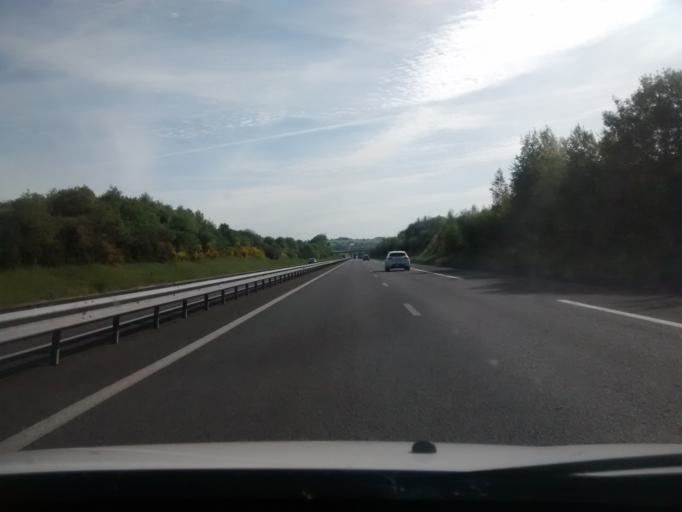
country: FR
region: Brittany
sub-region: Departement d'Ille-et-Vilaine
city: Saint-Jean-sur-Couesnon
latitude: 48.2884
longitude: -1.3812
